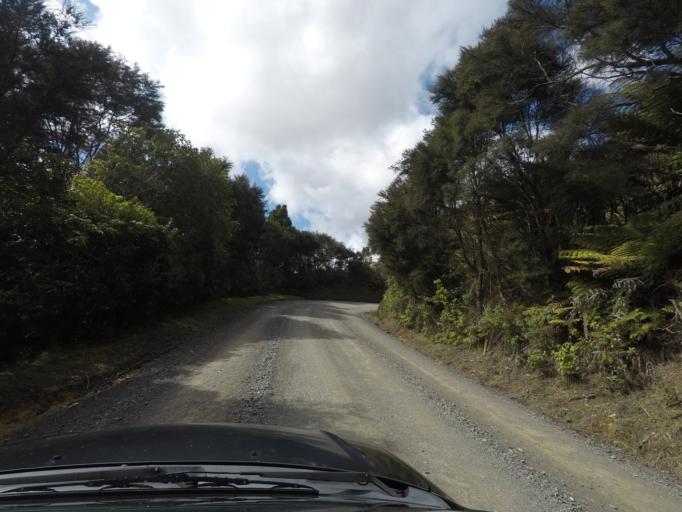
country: NZ
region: Auckland
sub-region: Auckland
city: Red Hill
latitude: -37.1124
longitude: 175.1301
